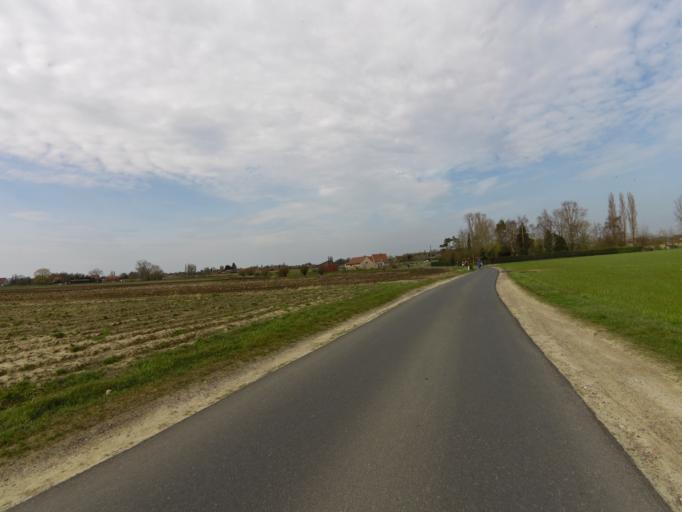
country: BE
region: Flanders
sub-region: Provincie West-Vlaanderen
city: Koekelare
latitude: 51.0795
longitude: 2.9779
